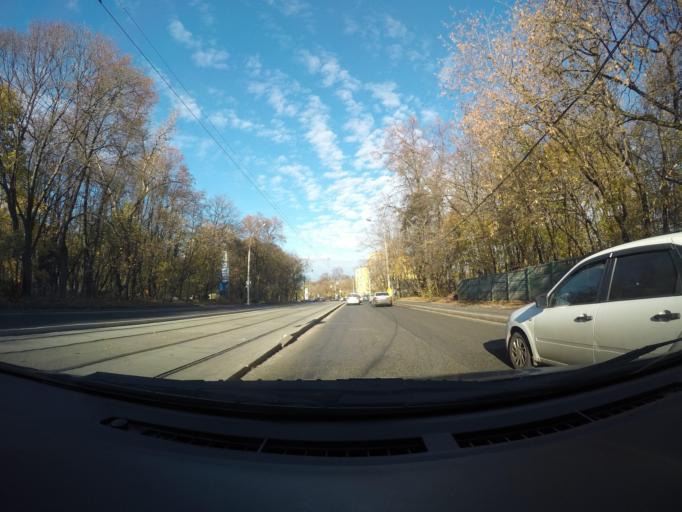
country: RU
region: Moscow
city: Sokol'niki
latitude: 55.8167
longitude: 37.6810
